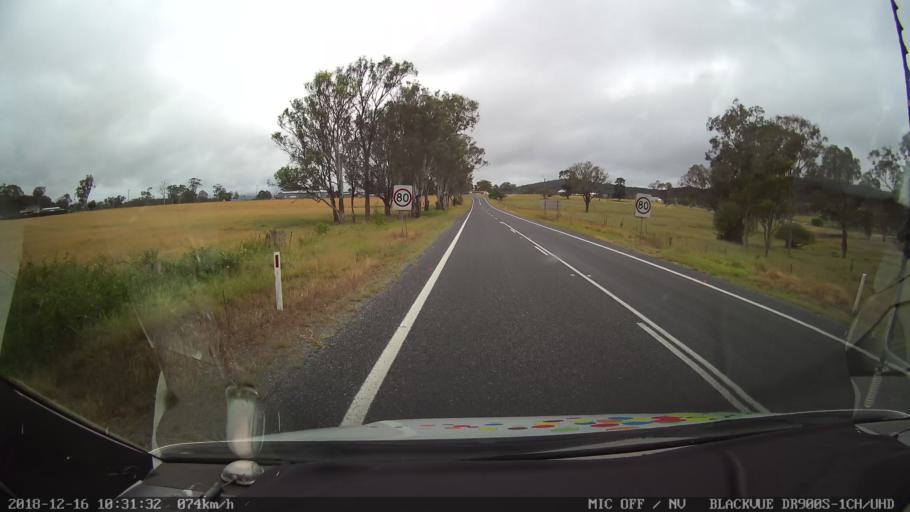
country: AU
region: New South Wales
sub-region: Tenterfield Municipality
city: Carrolls Creek
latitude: -29.0802
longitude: 152.0062
